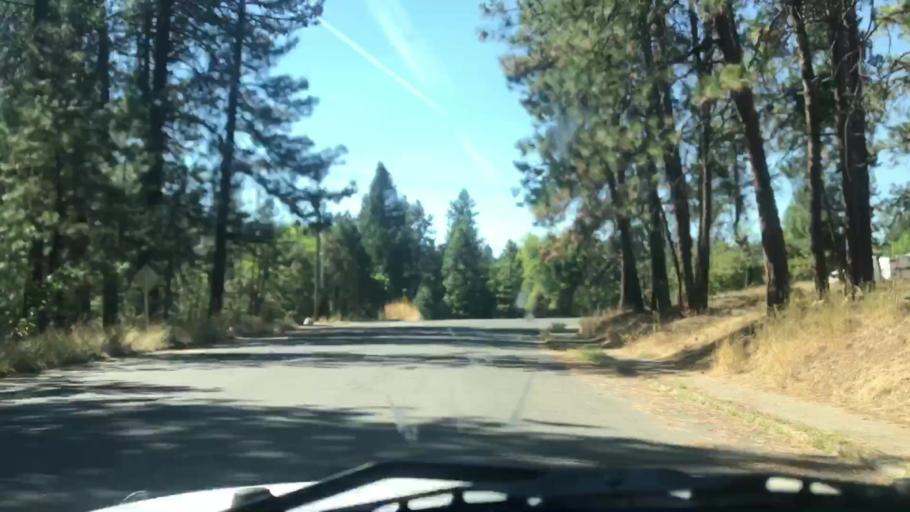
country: US
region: Washington
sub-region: Spokane County
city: Spokane
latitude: 47.6442
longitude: -117.4535
